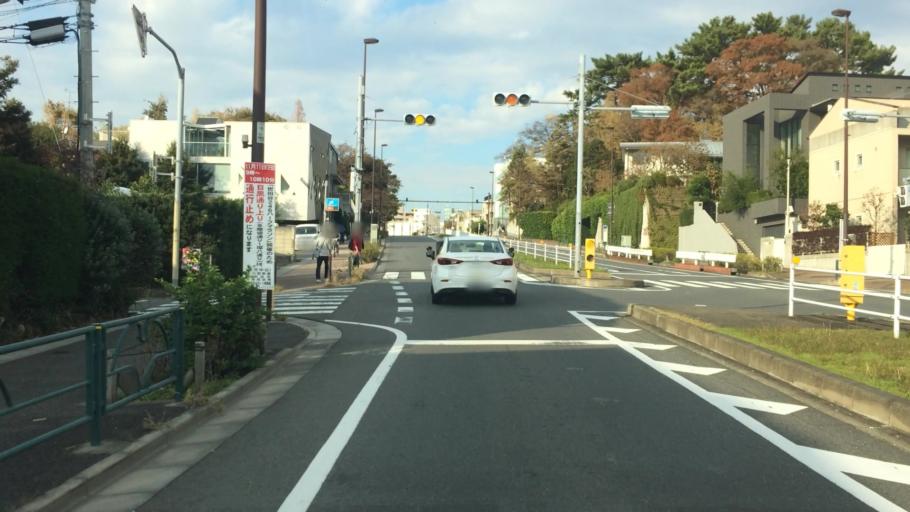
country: JP
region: Tokyo
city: Tokyo
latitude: 35.6019
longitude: 139.6473
